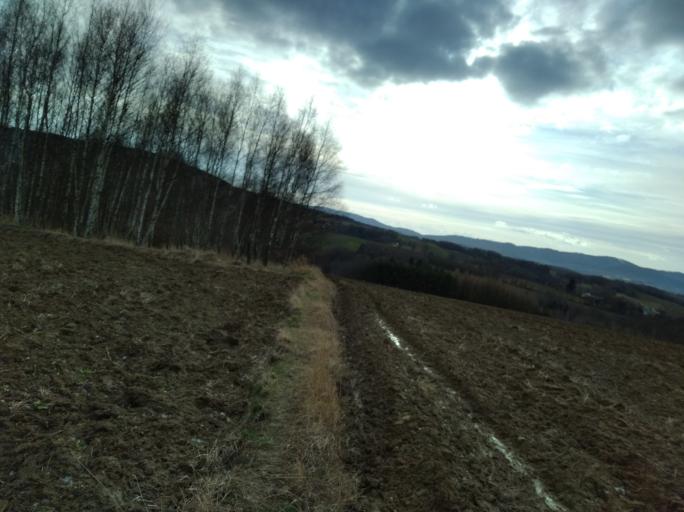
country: PL
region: Subcarpathian Voivodeship
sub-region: Powiat strzyzowski
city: Strzyzow
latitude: 49.8536
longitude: 21.7701
